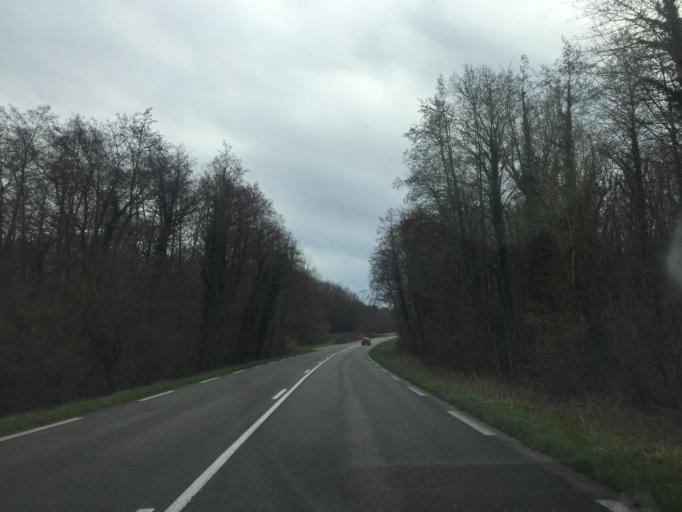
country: FR
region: Franche-Comte
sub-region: Departement du Jura
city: Mont-sous-Vaudrey
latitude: 46.8927
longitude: 5.5237
